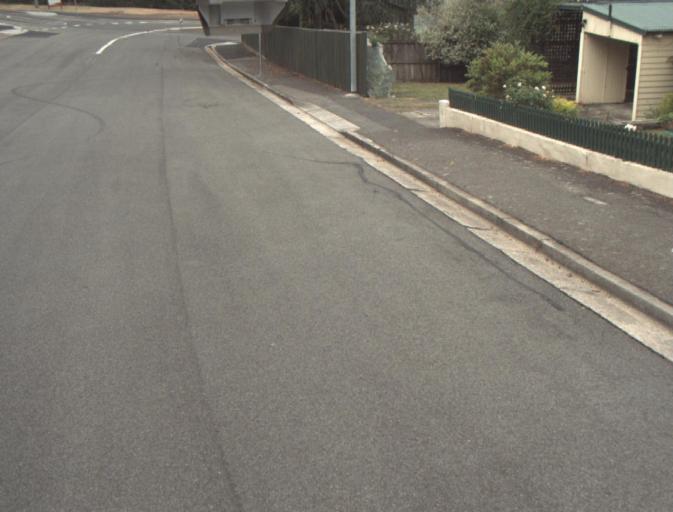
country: AU
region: Tasmania
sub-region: Launceston
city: Launceston
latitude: -41.4386
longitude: 147.1128
